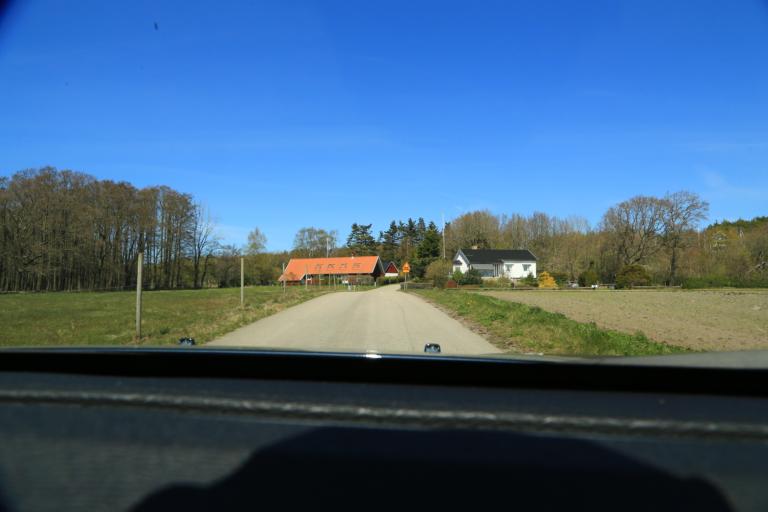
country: SE
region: Halland
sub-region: Varbergs Kommun
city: Traslovslage
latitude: 57.0902
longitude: 12.2880
